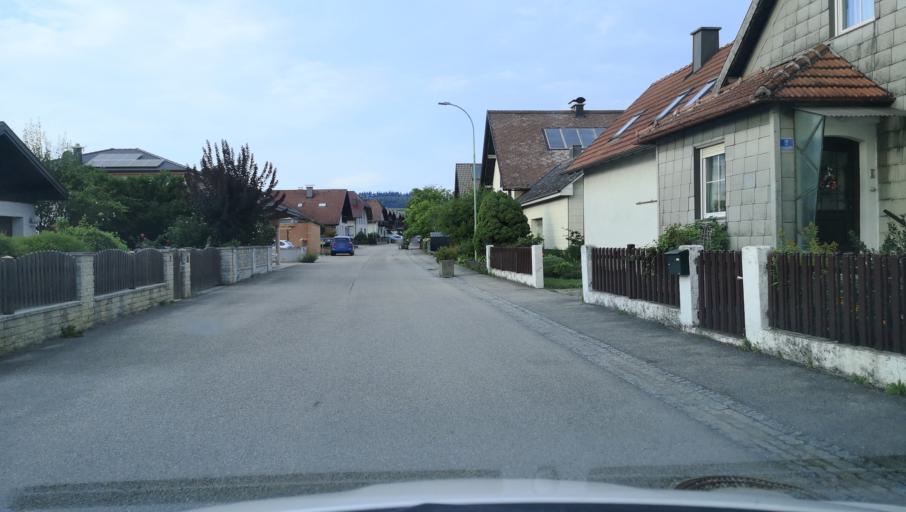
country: AT
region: Lower Austria
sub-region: Politischer Bezirk Melk
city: Blindenmarkt
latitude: 48.1285
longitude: 14.9833
